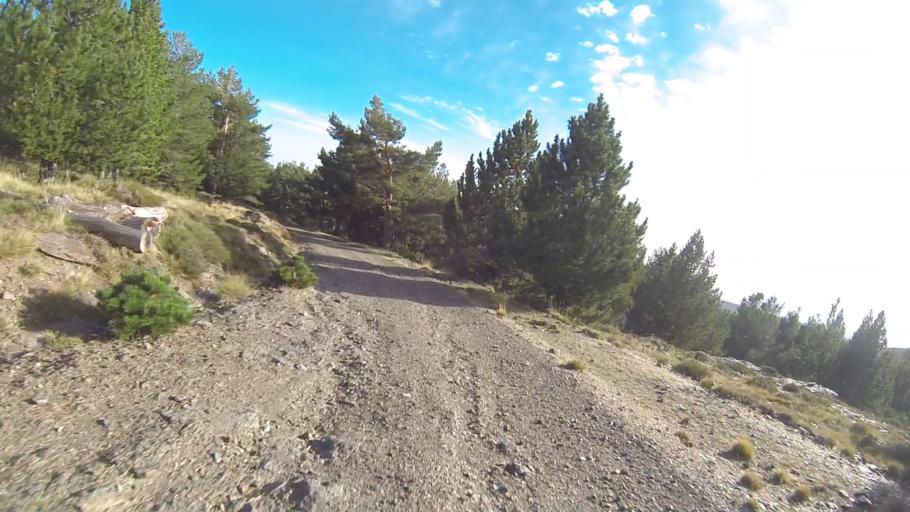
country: ES
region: Andalusia
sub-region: Provincia de Almeria
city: Paterna del Rio
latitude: 37.0839
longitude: -2.9045
